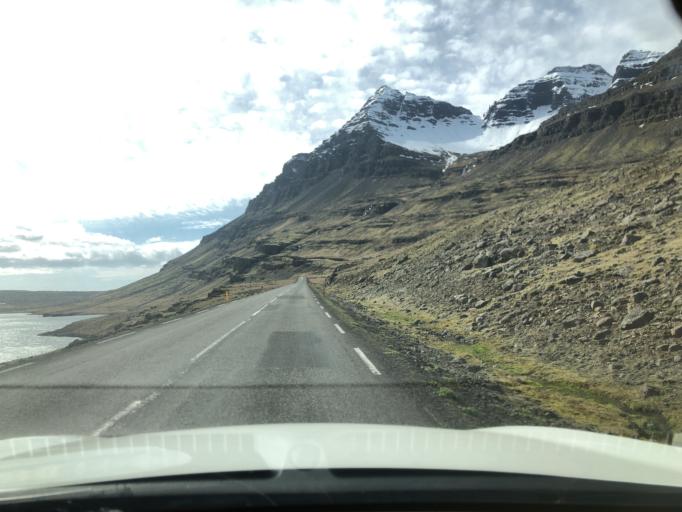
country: IS
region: East
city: Reydarfjoerdur
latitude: 64.7198
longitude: -14.4006
